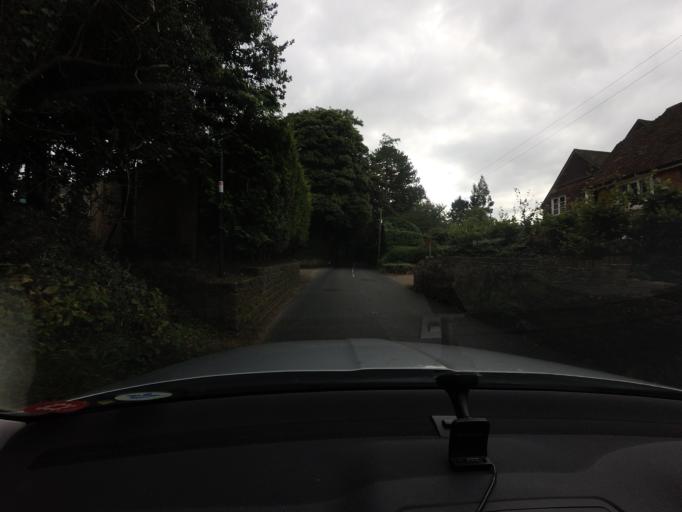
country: GB
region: England
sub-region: Kent
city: Borough Green
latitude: 51.2818
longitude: 0.2847
